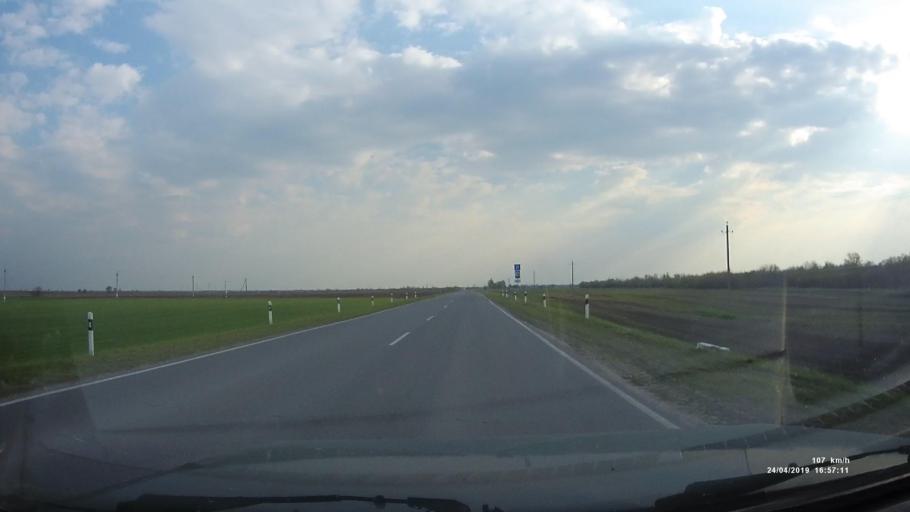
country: RU
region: Rostov
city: Proletarsk
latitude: 46.6404
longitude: 41.6708
